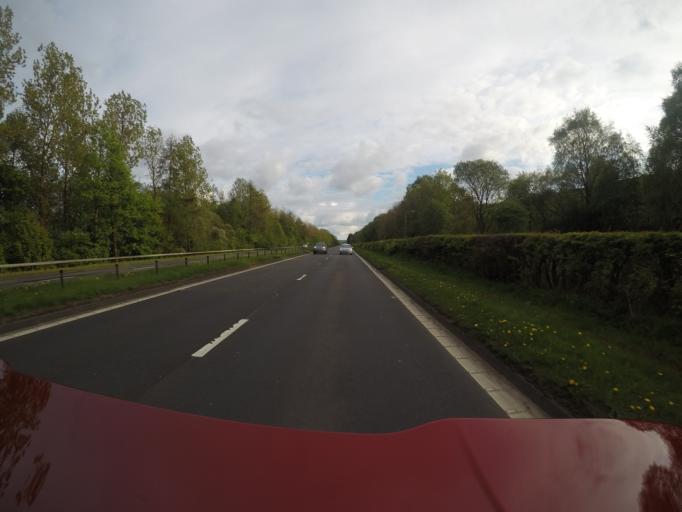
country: GB
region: Scotland
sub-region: West Dunbartonshire
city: Renton
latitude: 55.9742
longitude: -4.5877
